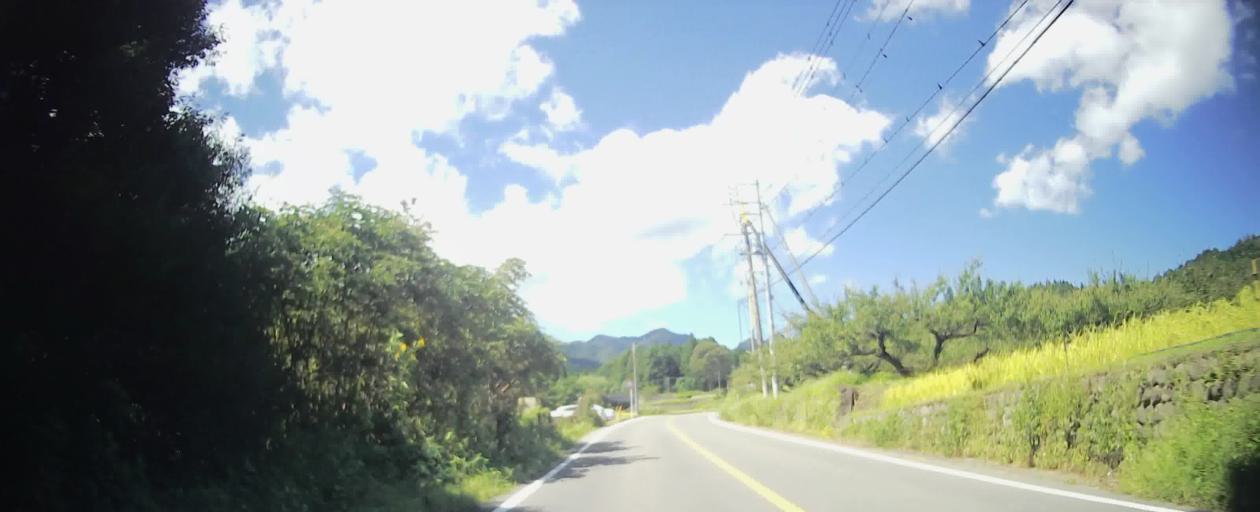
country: JP
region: Gunma
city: Kanekomachi
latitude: 36.4275
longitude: 138.9292
